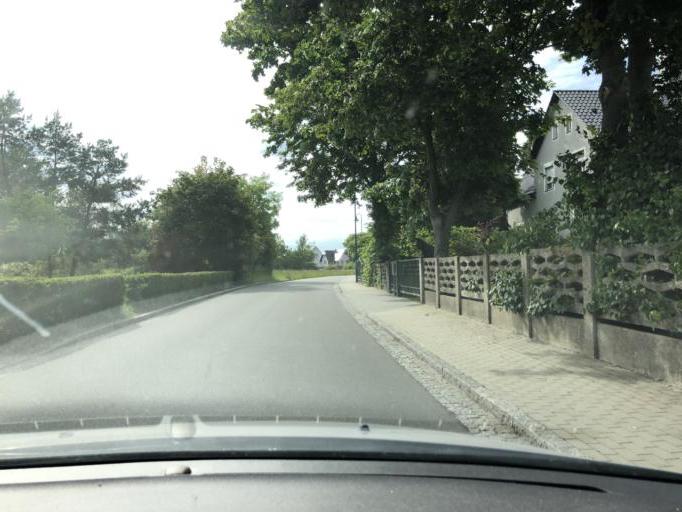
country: DE
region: Saxony
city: Grimma
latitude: 51.2919
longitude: 12.6860
